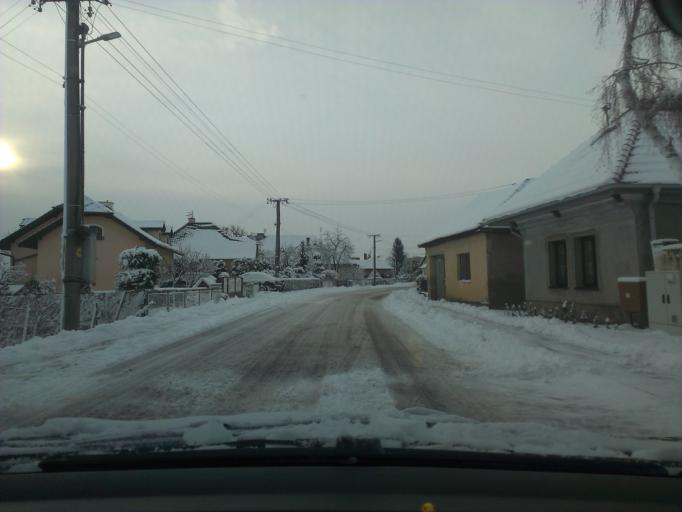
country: SK
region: Trnavsky
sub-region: Okres Trnava
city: Piestany
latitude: 48.5204
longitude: 17.9708
